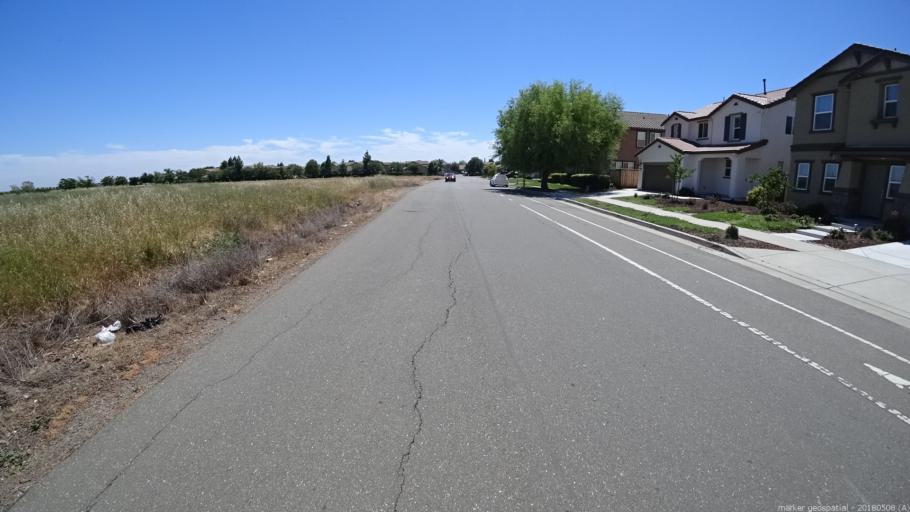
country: US
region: California
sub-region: Sacramento County
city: Elverta
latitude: 38.6679
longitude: -121.5273
